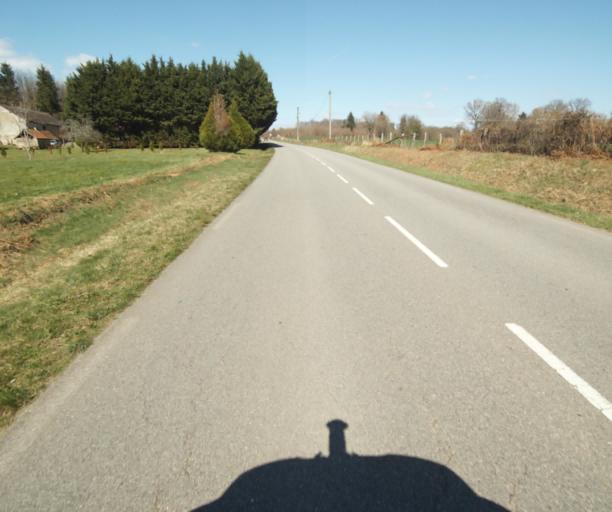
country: FR
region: Limousin
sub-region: Departement de la Correze
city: Saint-Mexant
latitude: 45.2959
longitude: 1.6706
